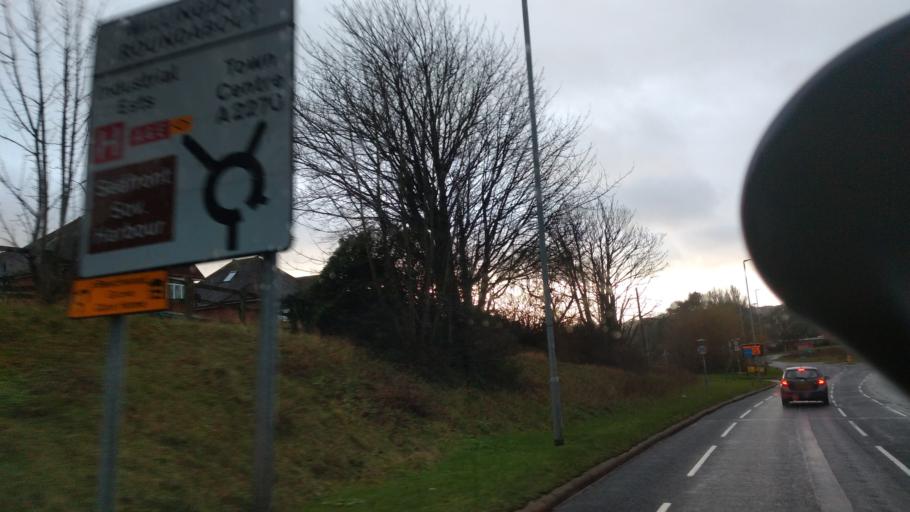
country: GB
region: England
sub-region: East Sussex
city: Eastbourne
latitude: 50.7966
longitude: 0.2573
